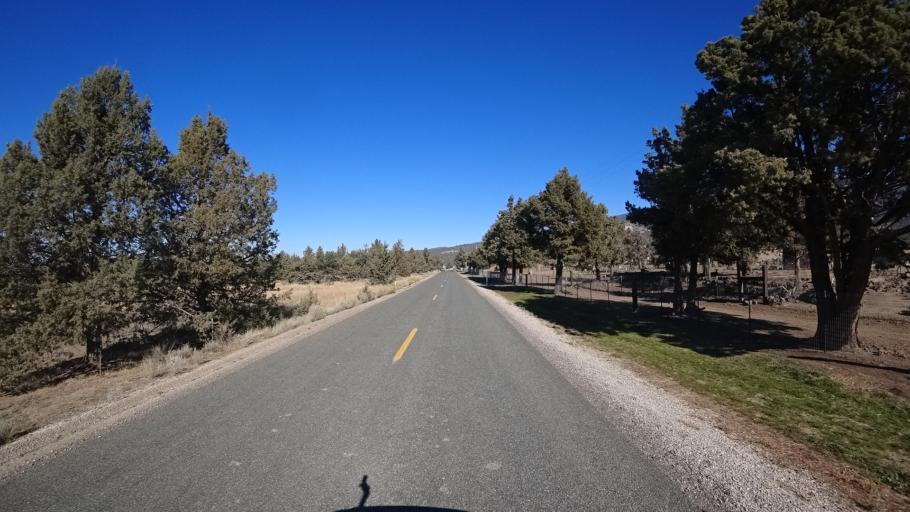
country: US
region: California
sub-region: Siskiyou County
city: Weed
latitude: 41.5908
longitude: -122.3017
